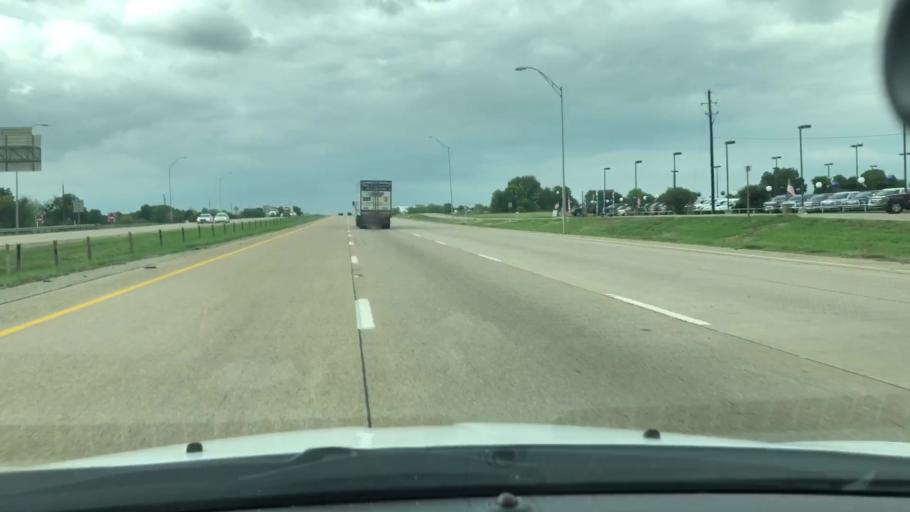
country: US
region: Texas
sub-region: Ellis County
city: Ennis
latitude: 32.3399
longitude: -96.6192
